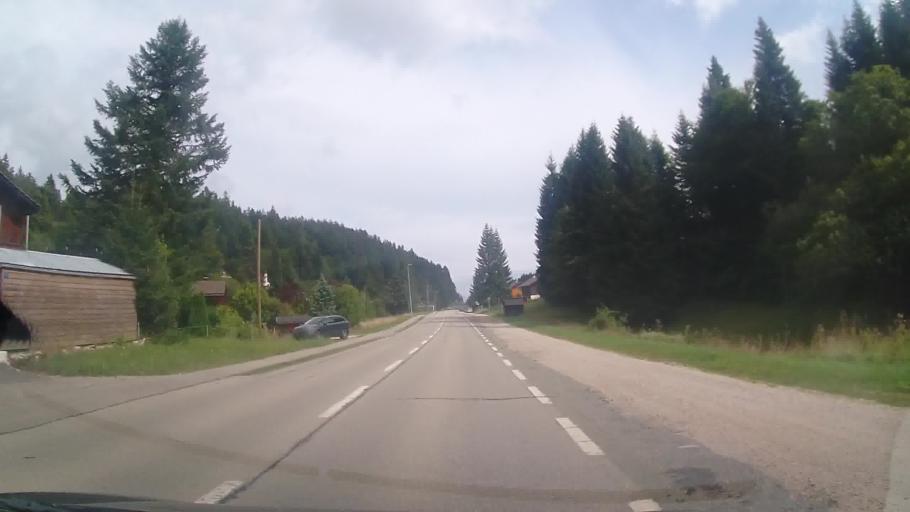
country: CH
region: Vaud
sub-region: Nyon District
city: Saint-Cergue
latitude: 46.4522
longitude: 6.1230
